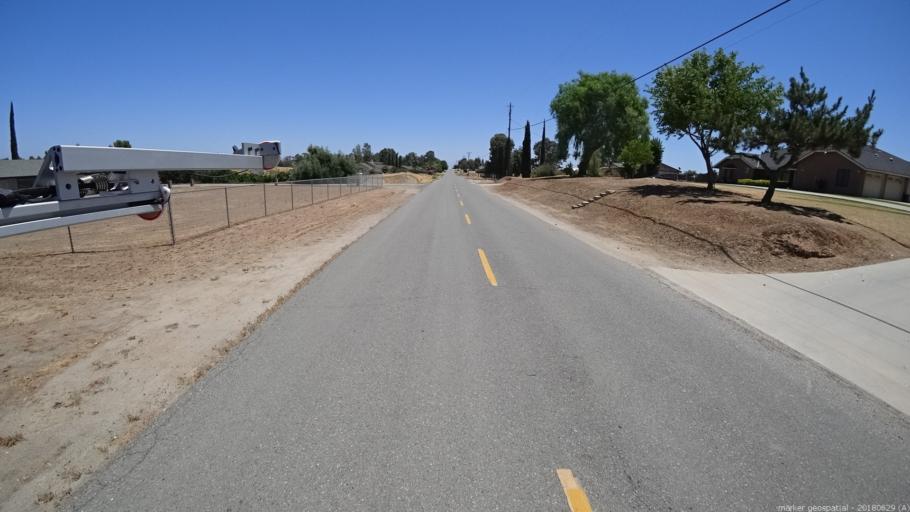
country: US
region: California
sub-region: Madera County
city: Parksdale
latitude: 36.9931
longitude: -119.9897
